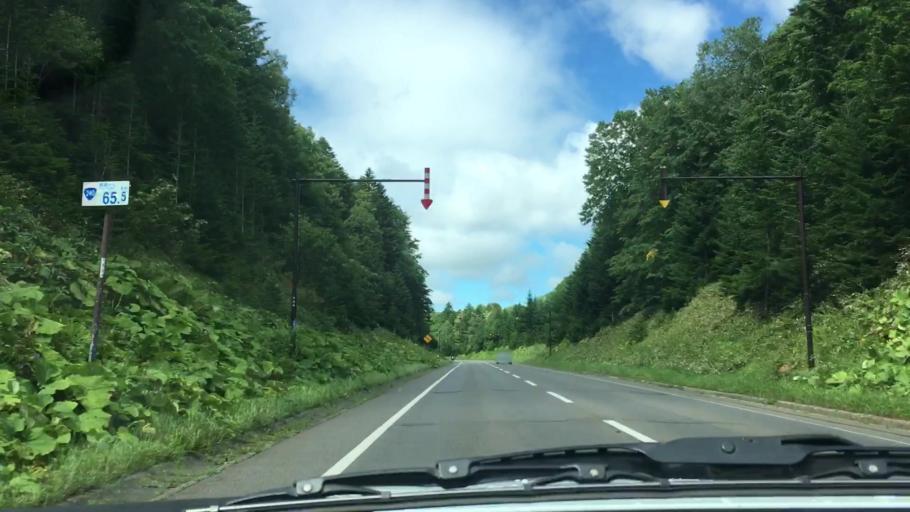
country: JP
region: Hokkaido
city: Bihoro
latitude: 43.4403
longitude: 144.0506
